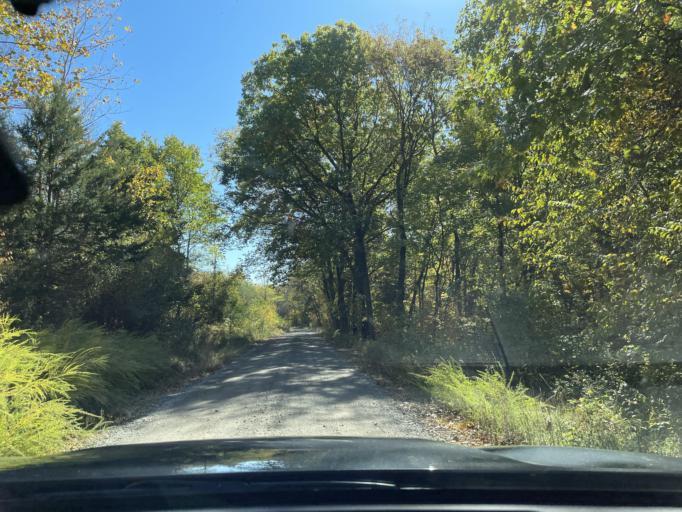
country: US
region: Missouri
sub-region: Andrew County
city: Savannah
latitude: 39.9393
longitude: -94.8697
